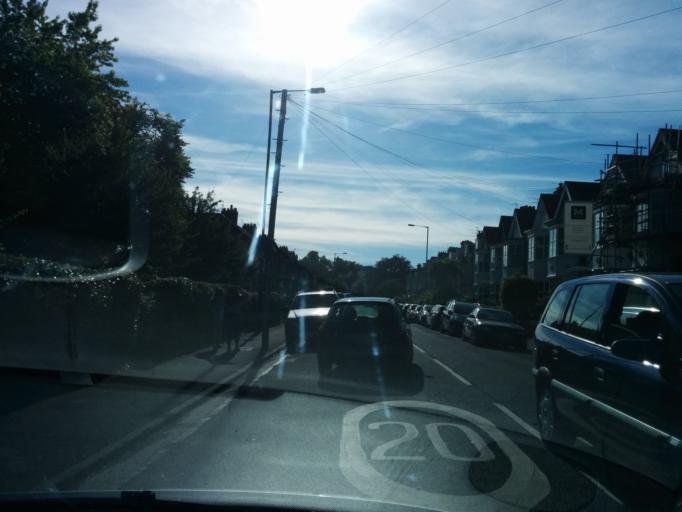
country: GB
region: England
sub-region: Bristol
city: Bristol
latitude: 51.4355
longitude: -2.5730
